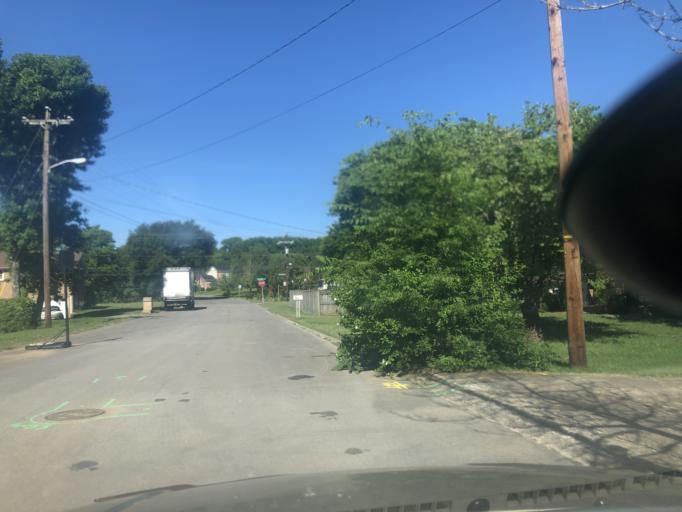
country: US
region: Tennessee
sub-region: Davidson County
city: Lakewood
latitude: 36.2499
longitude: -86.6693
